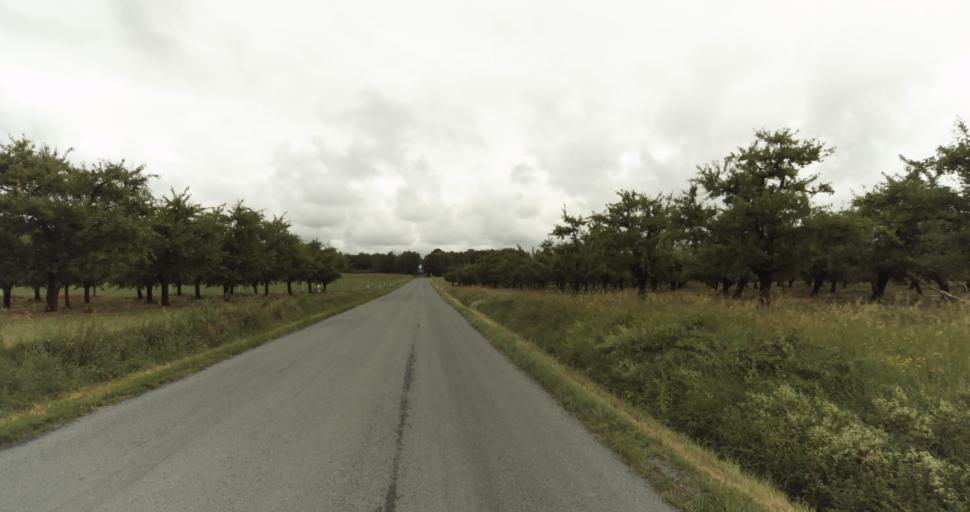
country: FR
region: Aquitaine
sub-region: Departement de la Dordogne
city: Beaumont-du-Perigord
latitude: 44.7074
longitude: 0.8274
